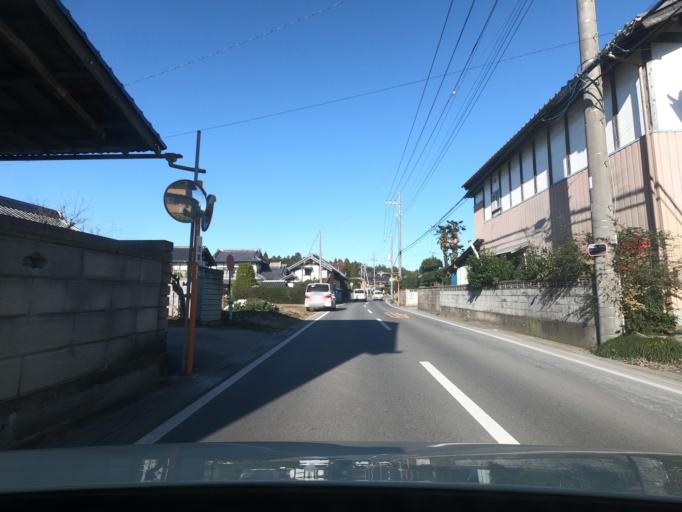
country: JP
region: Ibaraki
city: Ishige
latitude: 36.1179
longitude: 140.0582
